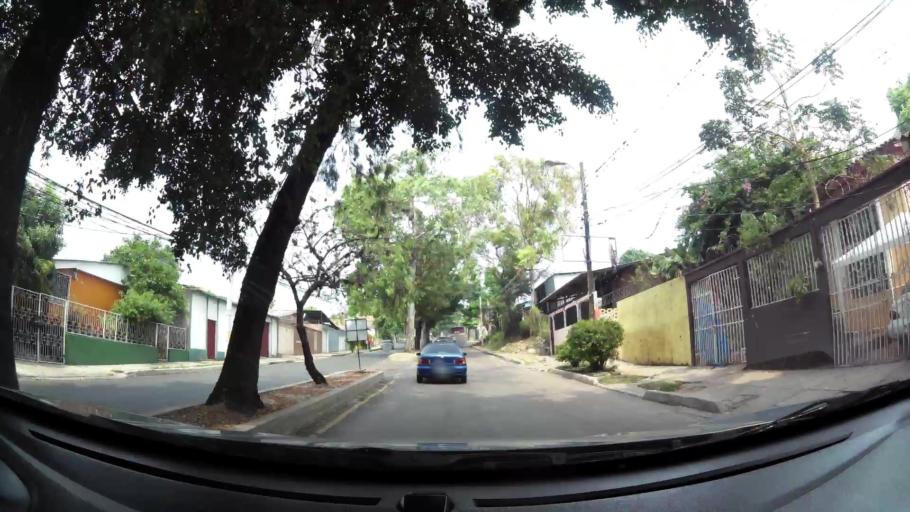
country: HN
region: Francisco Morazan
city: Tegucigalpa
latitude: 14.0727
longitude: -87.1929
